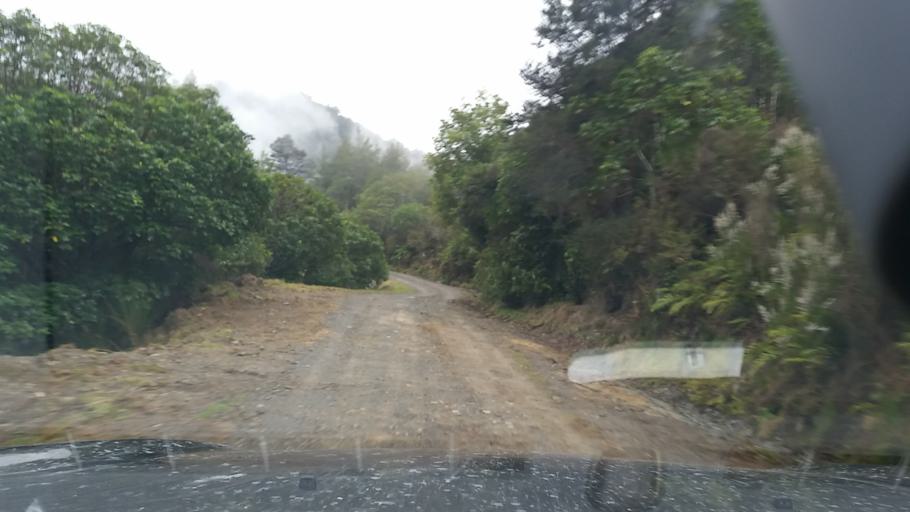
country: NZ
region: Nelson
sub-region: Nelson City
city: Nelson
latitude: -41.3765
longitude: 173.5942
